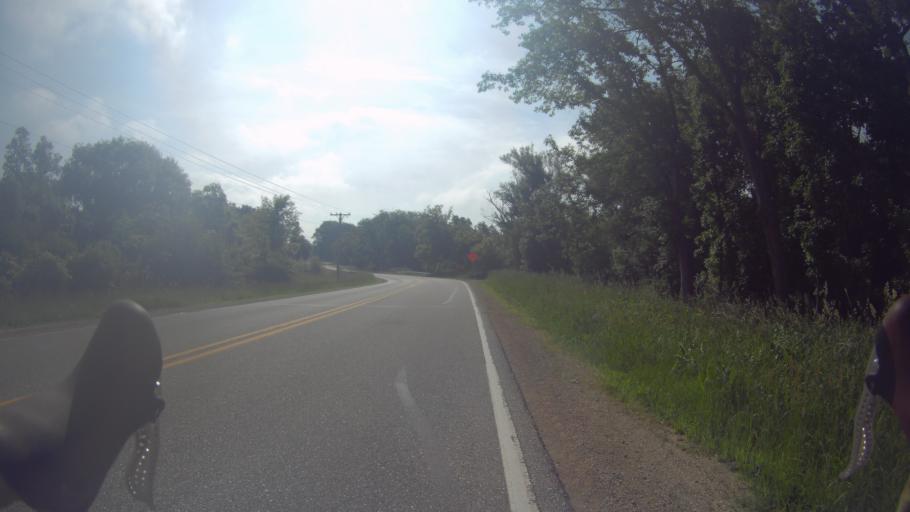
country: US
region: Wisconsin
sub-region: Dane County
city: McFarland
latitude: 43.0131
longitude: -89.2377
